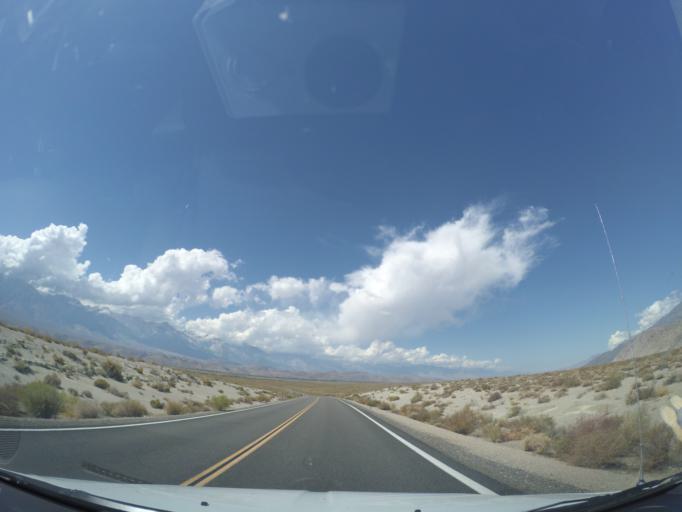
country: US
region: California
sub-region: Inyo County
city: Lone Pine
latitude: 36.5725
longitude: -117.9918
